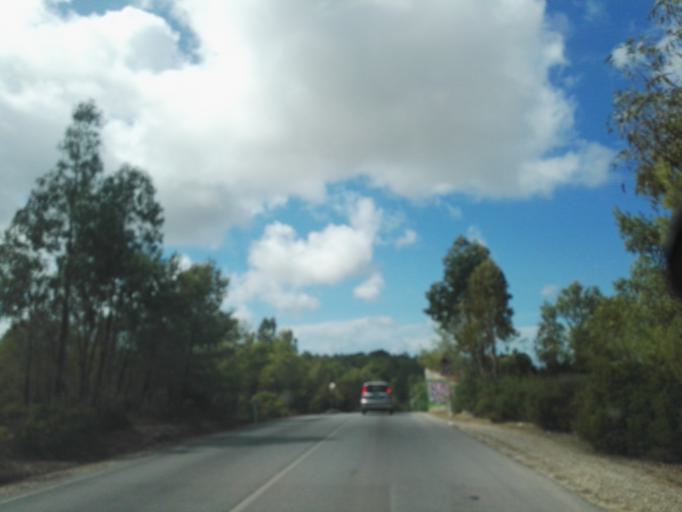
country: PT
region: Setubal
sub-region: Sesimbra
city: Sesimbra
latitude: 38.4612
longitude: -9.0950
